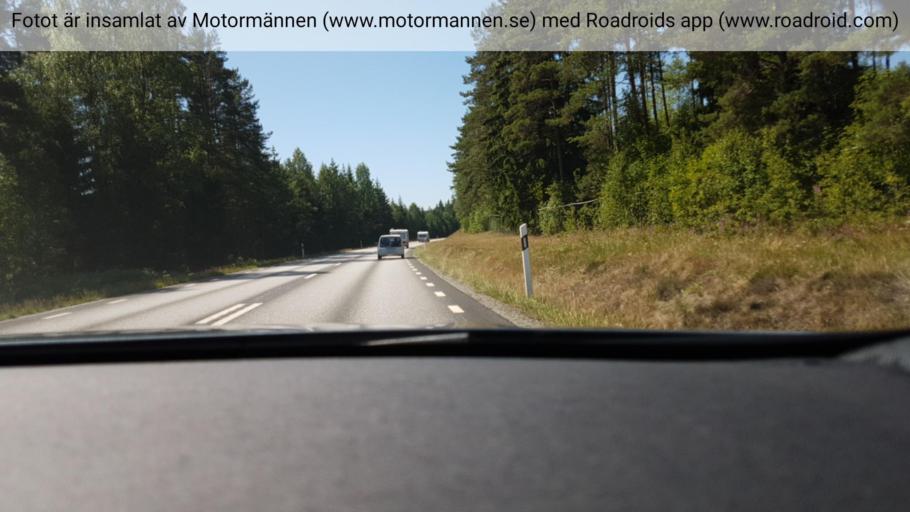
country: SE
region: Joenkoeping
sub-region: Gnosjo Kommun
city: Gnosjoe
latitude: 57.5195
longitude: 13.6826
